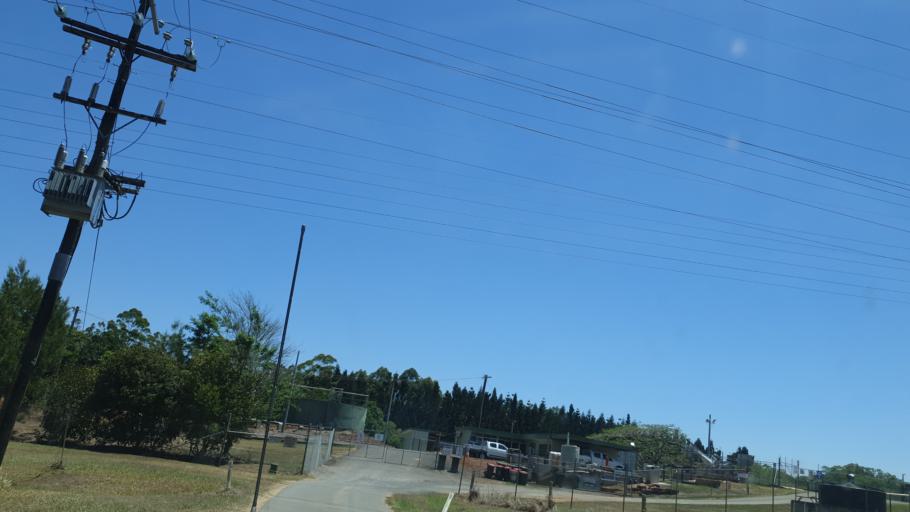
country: AU
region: Queensland
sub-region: Tablelands
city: Atherton
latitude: -17.2551
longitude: 145.4799
